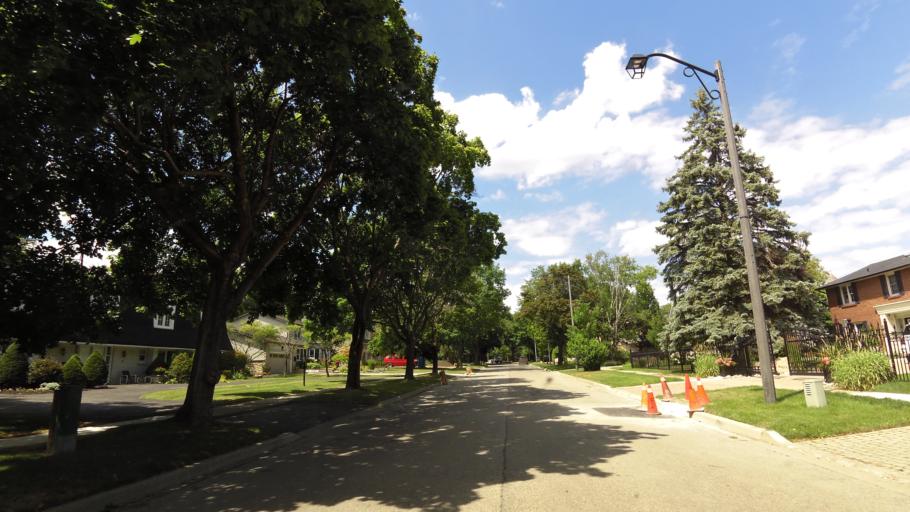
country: CA
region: Ontario
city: Mississauga
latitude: 43.5134
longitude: -79.6026
